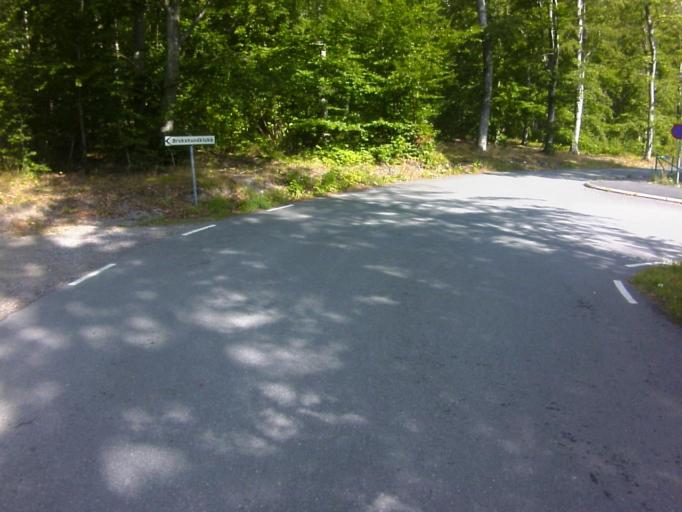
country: SE
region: Blekinge
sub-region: Solvesborgs Kommun
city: Soelvesborg
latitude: 56.0581
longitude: 14.5794
